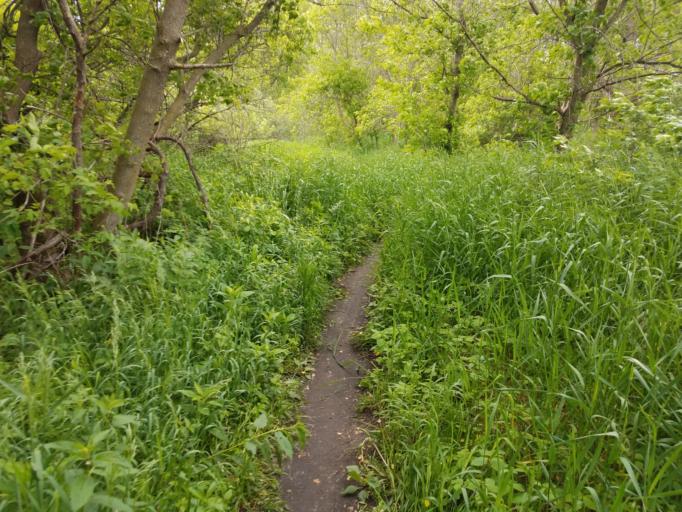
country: US
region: Minnesota
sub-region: Olmsted County
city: Rochester
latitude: 43.9543
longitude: -92.4363
